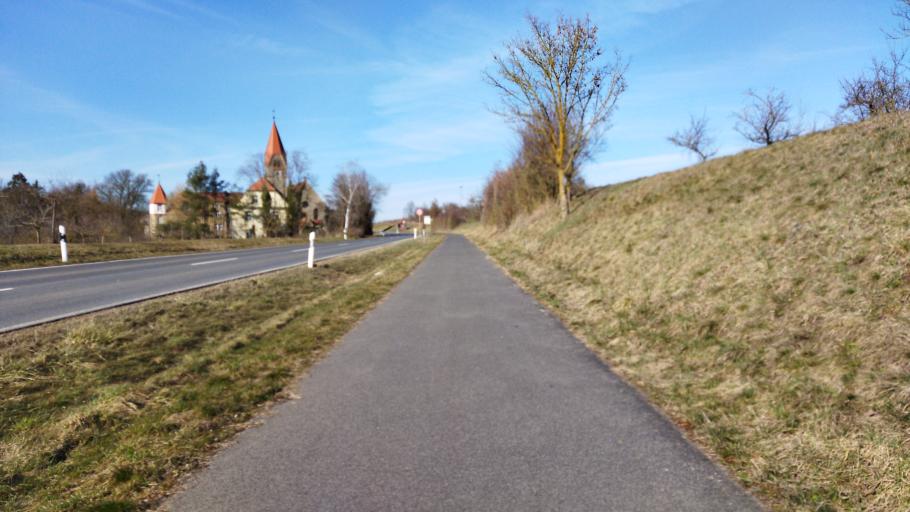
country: DE
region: Bavaria
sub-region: Regierungsbezirk Unterfranken
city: Wipfeld
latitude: 49.9235
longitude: 10.1864
